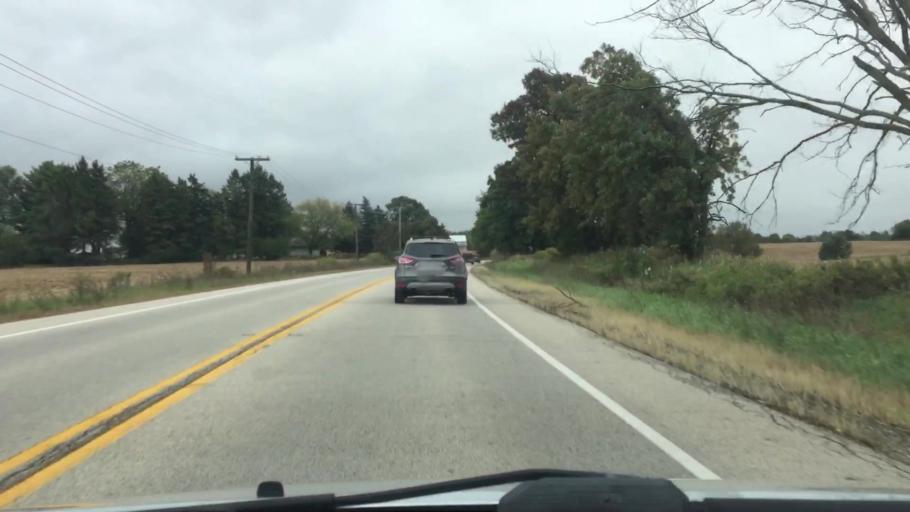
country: US
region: Illinois
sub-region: McHenry County
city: McCullom Lake
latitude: 42.3873
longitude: -88.2819
